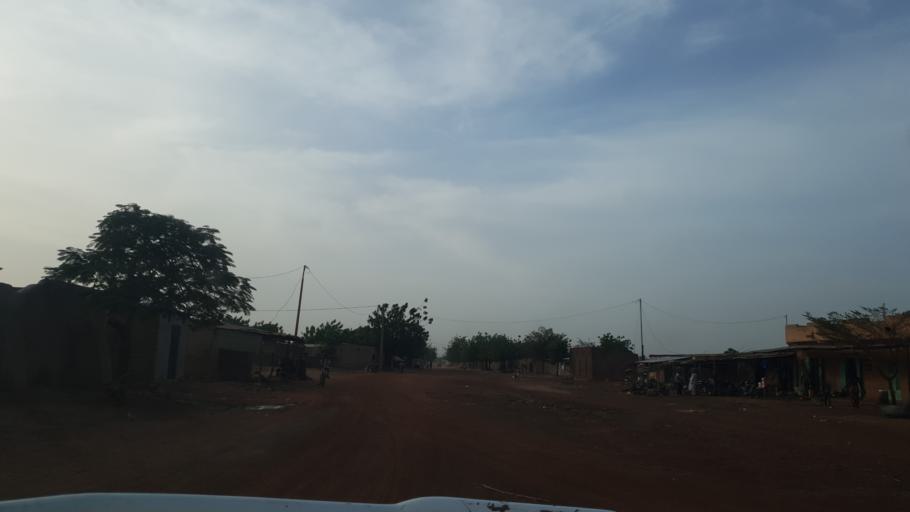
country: ML
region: Segou
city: Baroueli
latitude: 12.7809
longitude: -6.9442
